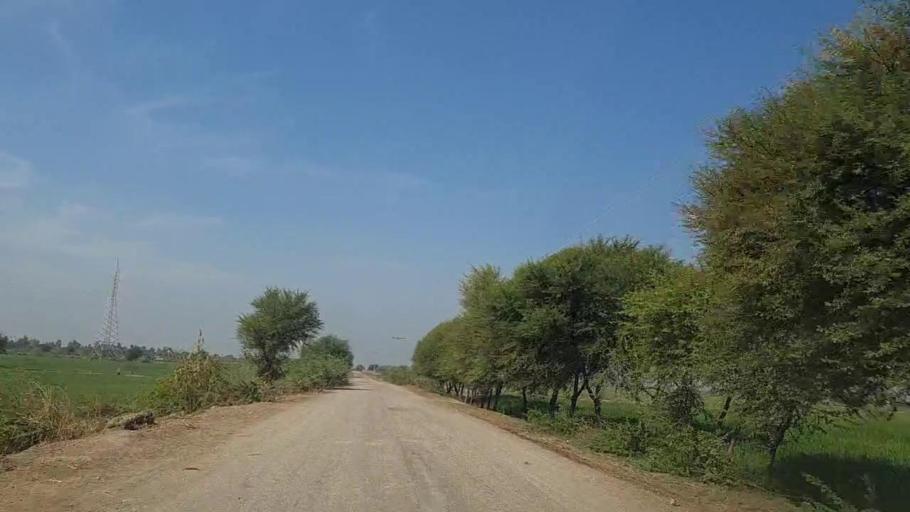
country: PK
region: Sindh
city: Mirpur Khas
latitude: 25.4825
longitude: 68.9808
